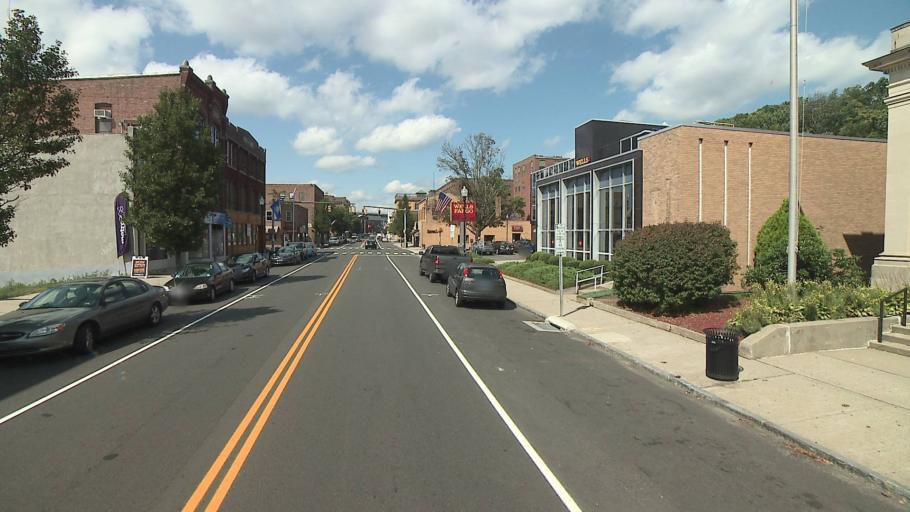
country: US
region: Connecticut
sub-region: New Haven County
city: Ansonia
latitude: 41.3432
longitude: -73.0787
